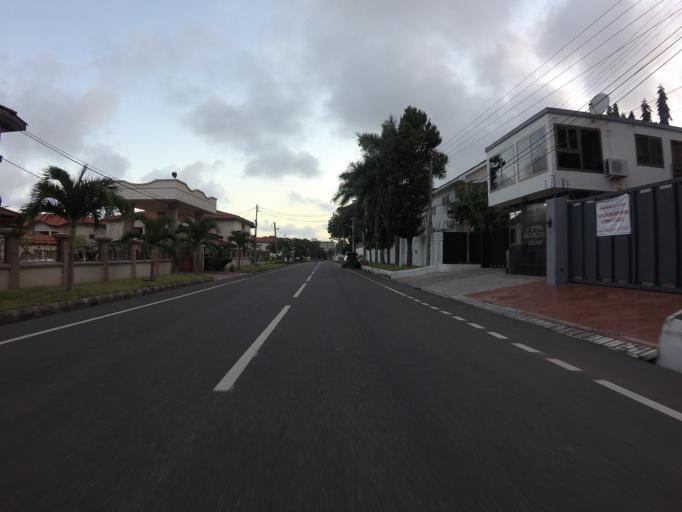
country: GH
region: Greater Accra
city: Accra
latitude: 5.5749
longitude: -0.1854
